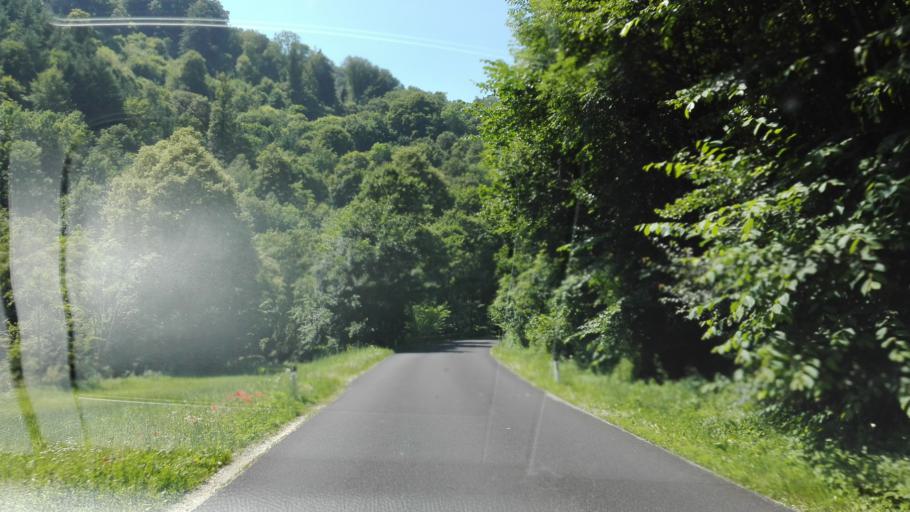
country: AT
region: Upper Austria
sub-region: Politischer Bezirk Rohrbach
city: Kleinzell im Muehlkreis
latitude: 48.3742
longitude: 13.9441
